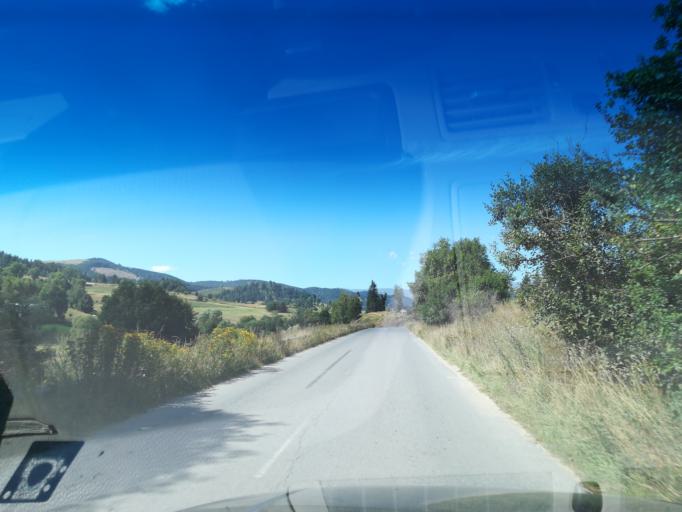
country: BG
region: Sofiya
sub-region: Obshtina Koprivshtitsa
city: Koprivshtitsa
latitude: 42.6114
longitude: 24.3753
